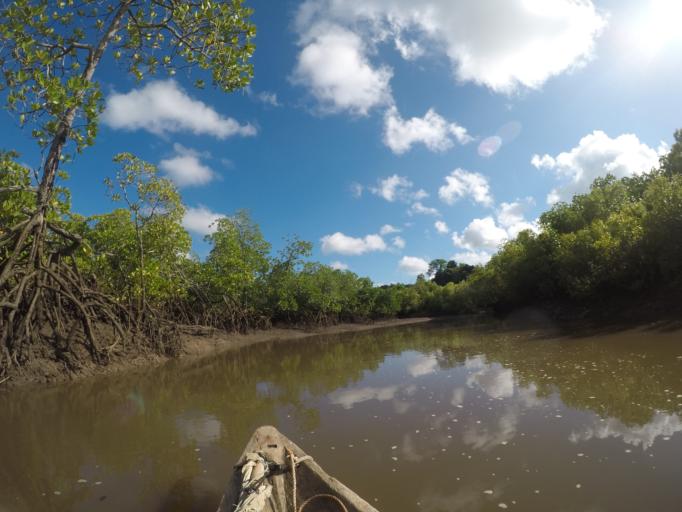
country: TZ
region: Pemba South
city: Mtambile
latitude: -5.3452
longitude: 39.6960
